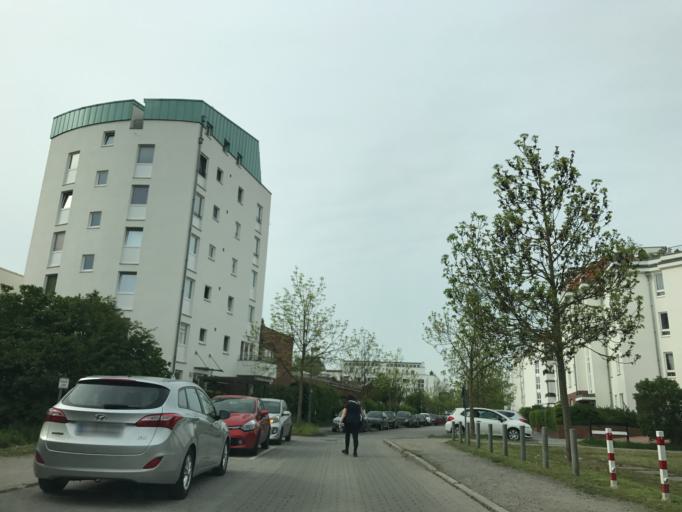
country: DE
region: Berlin
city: Staaken
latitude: 52.5254
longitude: 13.1491
